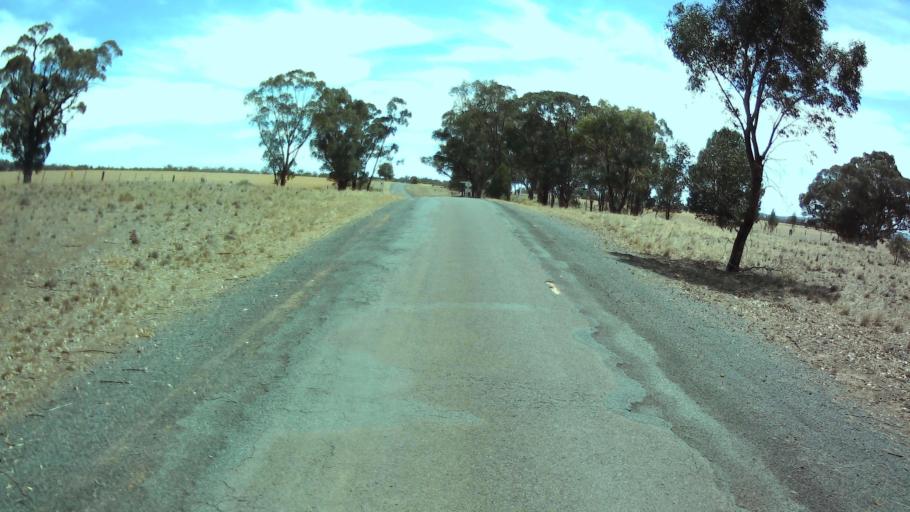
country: AU
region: New South Wales
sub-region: Weddin
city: Grenfell
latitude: -33.7504
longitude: 148.2071
